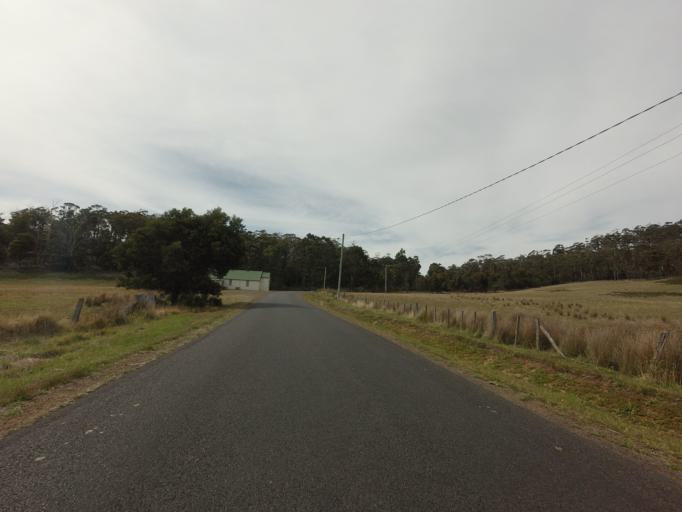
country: AU
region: Tasmania
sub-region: Sorell
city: Sorell
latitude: -42.4702
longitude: 147.5706
